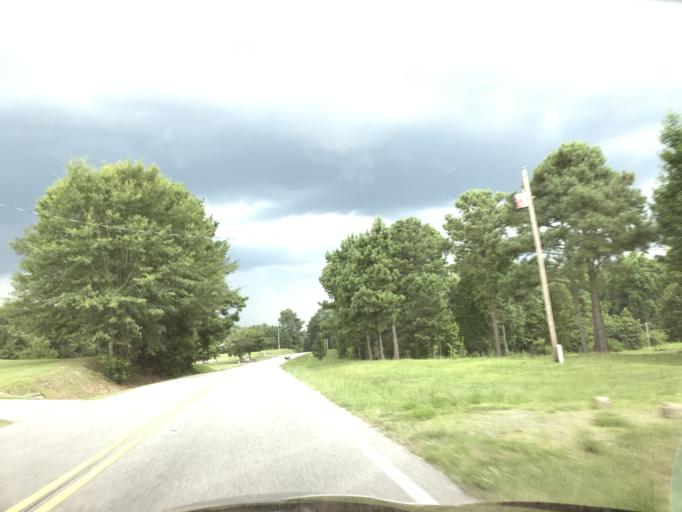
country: US
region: North Carolina
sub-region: Johnston County
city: Four Oaks
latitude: 35.5113
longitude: -78.4733
